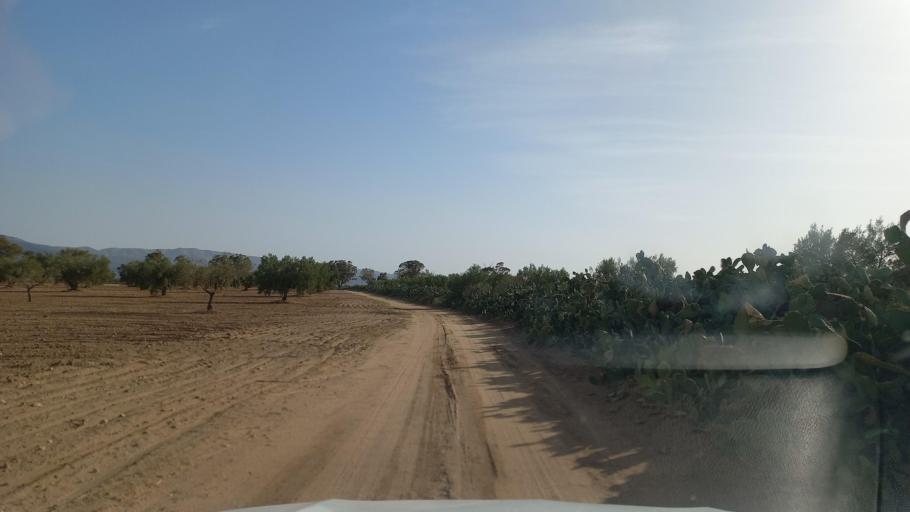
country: TN
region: Al Qasrayn
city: Kasserine
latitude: 35.2261
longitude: 8.9394
